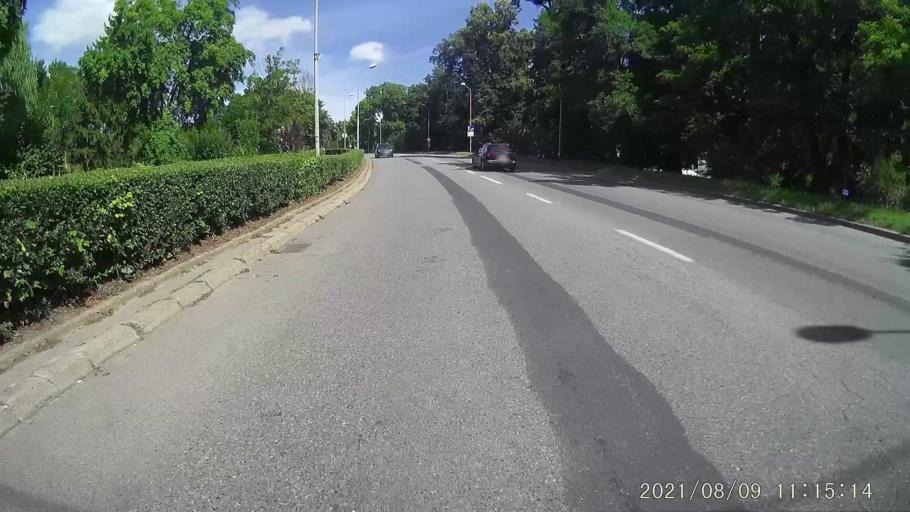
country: PL
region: Lower Silesian Voivodeship
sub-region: Powiat klodzki
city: Klodzko
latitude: 50.4384
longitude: 16.6489
